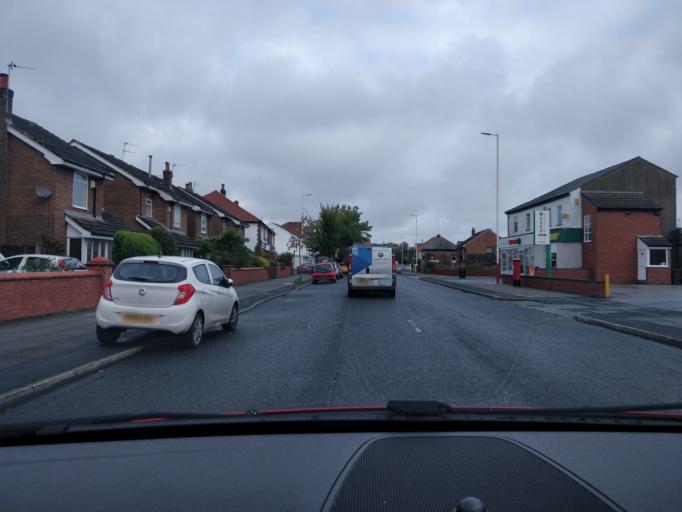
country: GB
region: England
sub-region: Sefton
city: Southport
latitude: 53.6185
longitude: -3.0159
